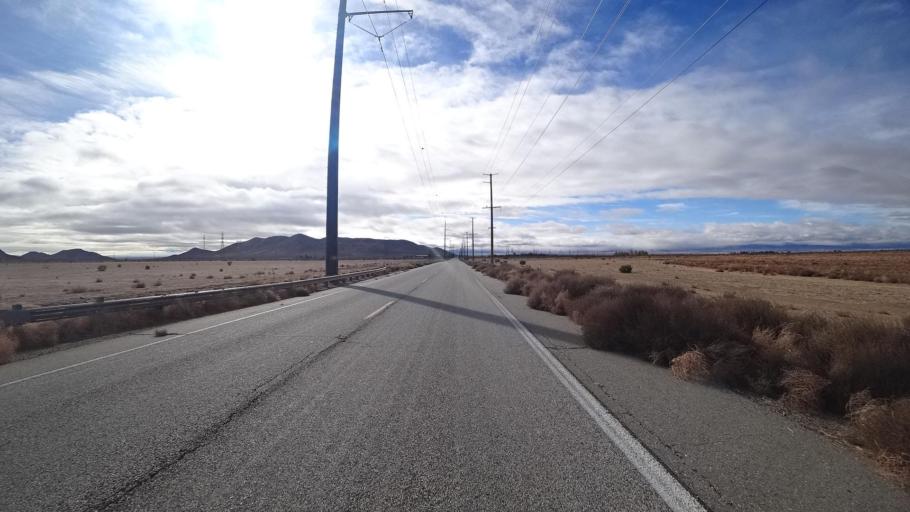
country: US
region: California
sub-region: Kern County
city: Rosamond
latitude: 34.9103
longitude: -118.2913
